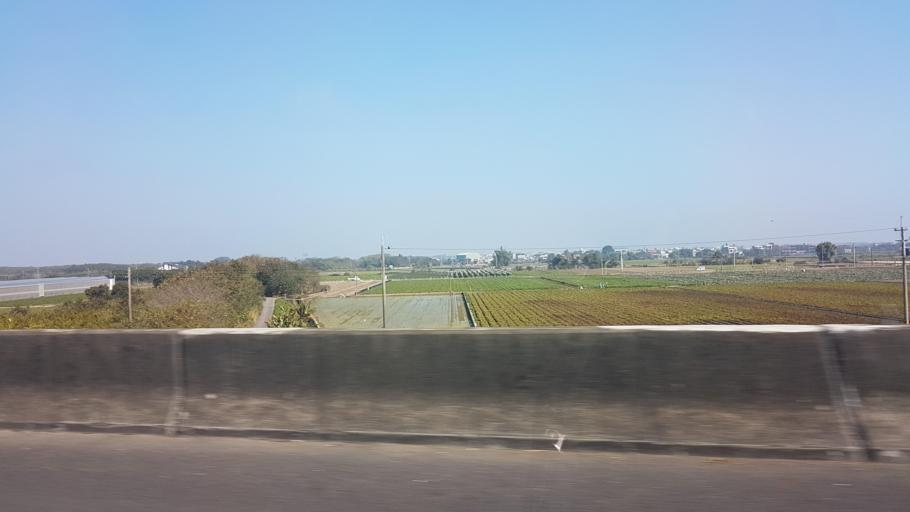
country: TW
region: Taiwan
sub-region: Chiayi
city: Taibao
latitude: 23.4217
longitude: 120.3698
